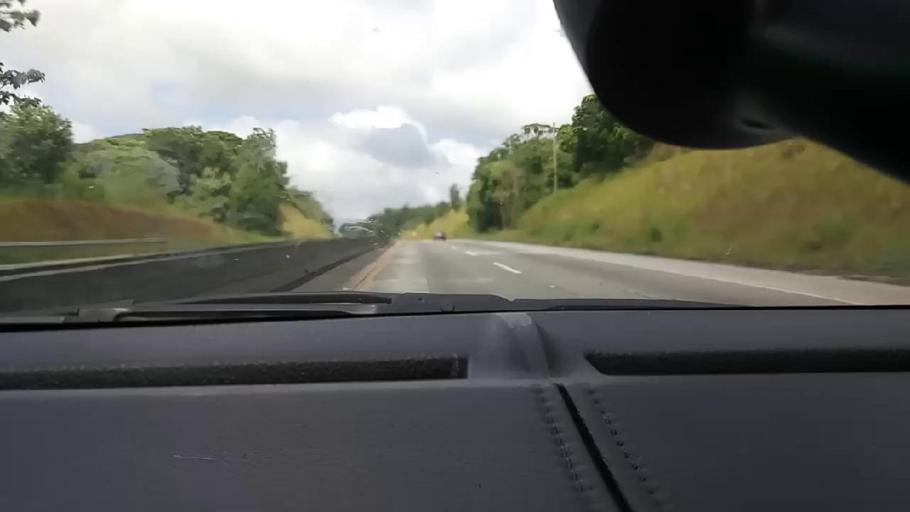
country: PA
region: Colon
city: Rio Rita
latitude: 9.2944
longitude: -79.7841
